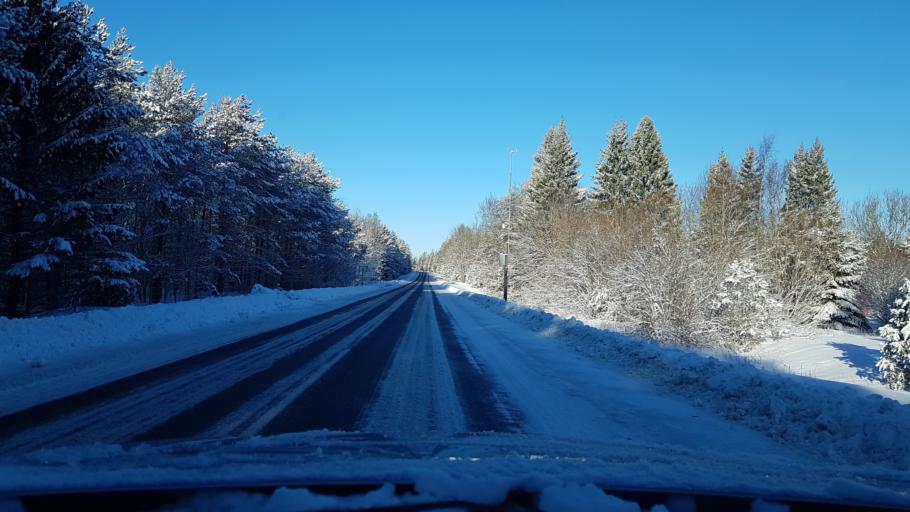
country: EE
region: Hiiumaa
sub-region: Kaerdla linn
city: Kardla
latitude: 58.9718
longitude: 22.8245
